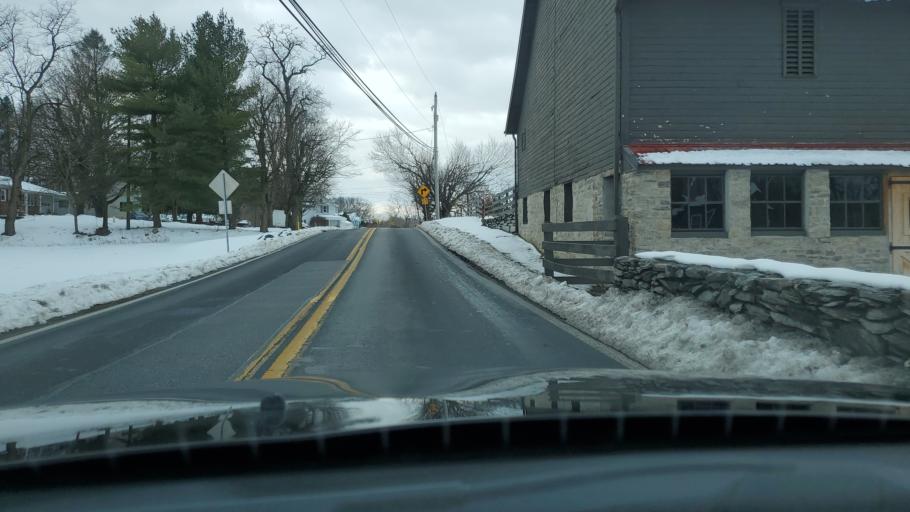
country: US
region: Pennsylvania
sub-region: Cumberland County
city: Mechanicsburg
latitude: 40.2189
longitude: -77.0456
